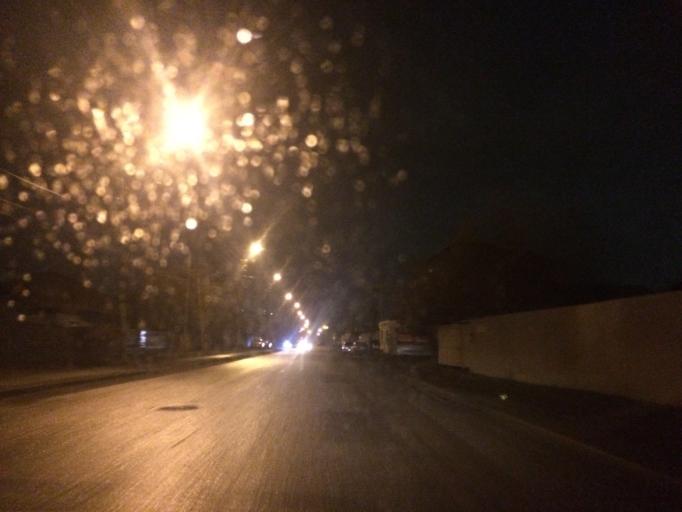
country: KZ
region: Astana Qalasy
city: Astana
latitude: 51.1884
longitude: 71.3844
